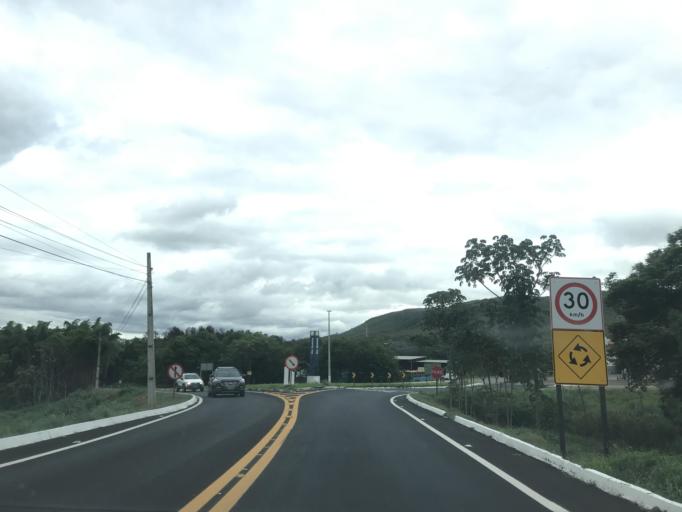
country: BR
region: Goias
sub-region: Caldas Novas
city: Caldas Novas
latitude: -17.7650
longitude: -48.7553
